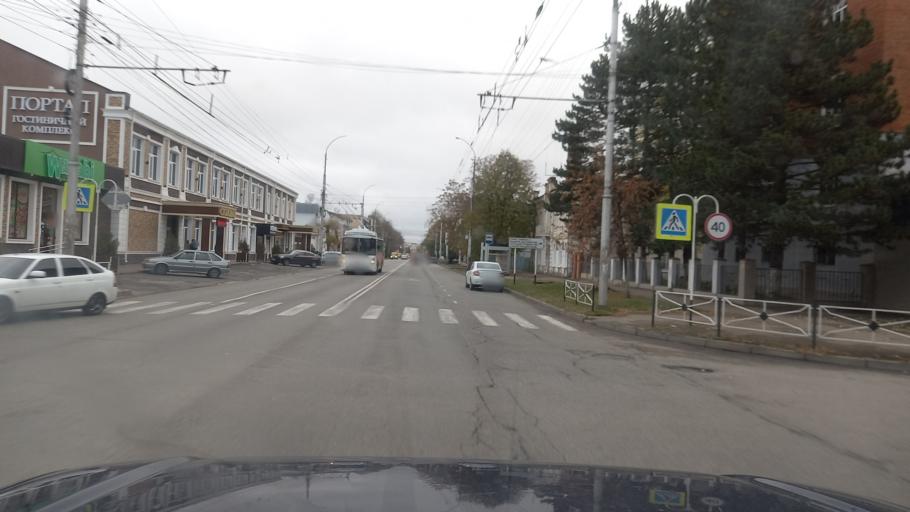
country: RU
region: Adygeya
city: Maykop
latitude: 44.6138
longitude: 40.1085
